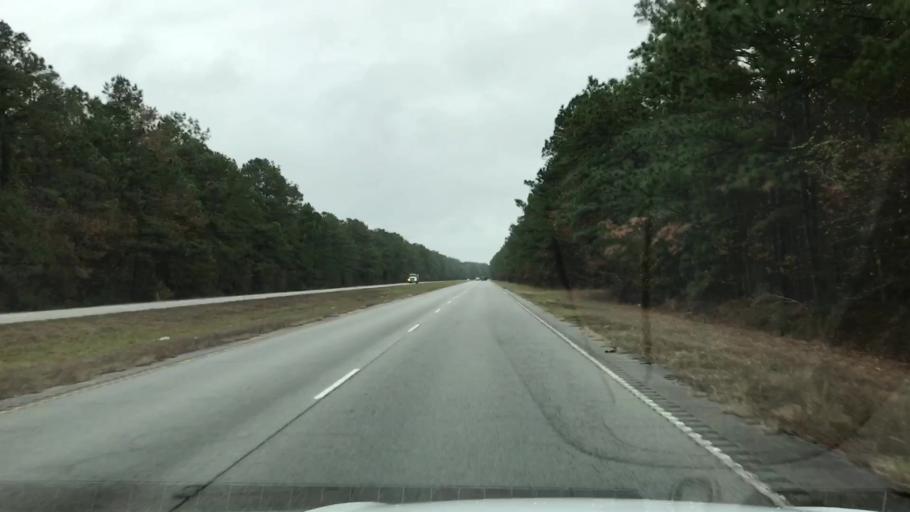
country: US
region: South Carolina
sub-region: Charleston County
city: Awendaw
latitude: 32.9657
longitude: -79.6813
